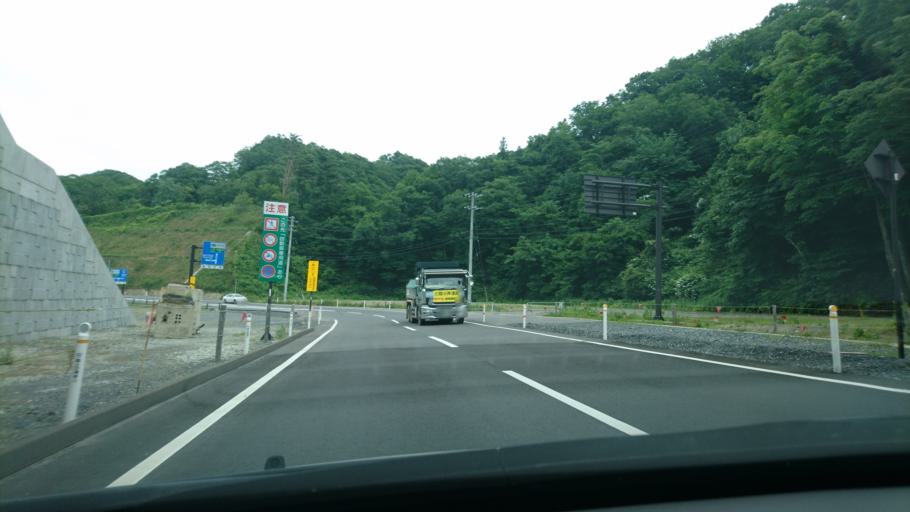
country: JP
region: Iwate
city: Miyako
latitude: 39.9915
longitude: 141.8781
